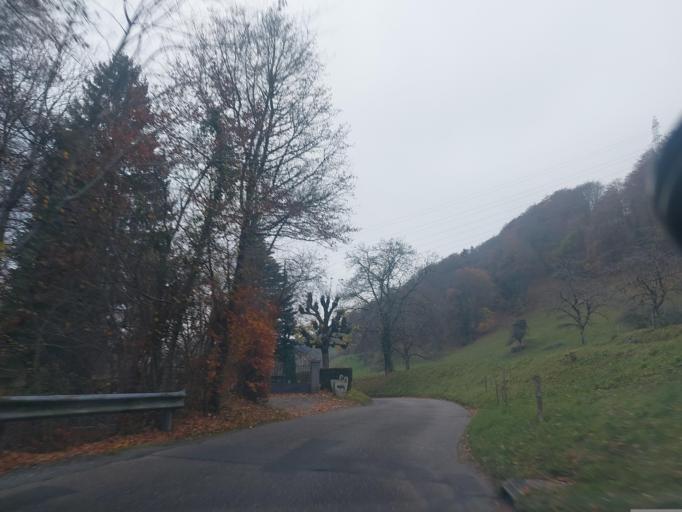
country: CH
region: Vaud
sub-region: Riviera-Pays-d'Enhaut District
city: Blonay
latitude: 46.4959
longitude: 6.8797
